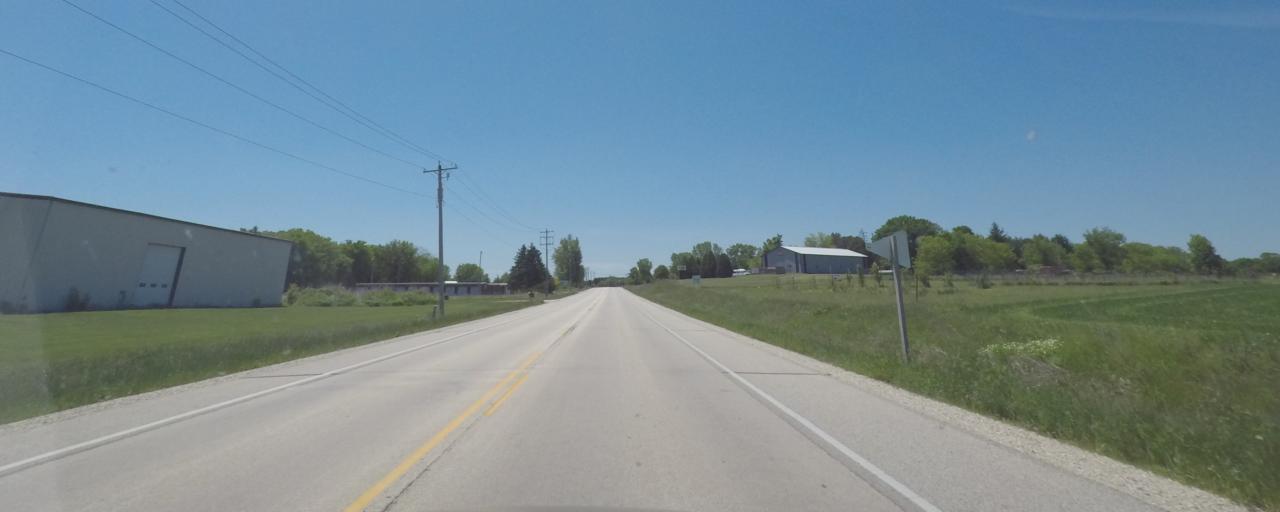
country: US
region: Wisconsin
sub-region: Ozaukee County
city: Kohler
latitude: 43.5403
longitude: -88.0881
